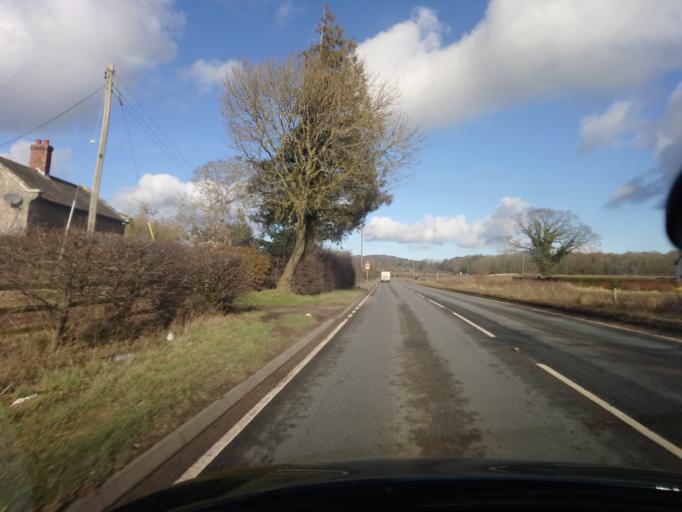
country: GB
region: England
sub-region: Shropshire
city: Clive
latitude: 52.7943
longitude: -2.7016
